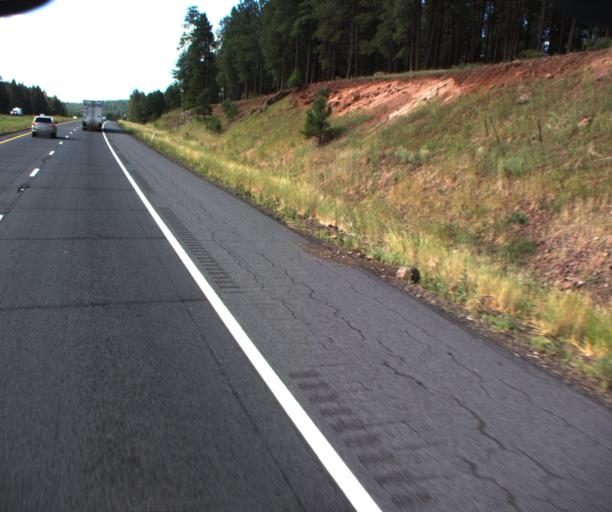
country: US
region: Arizona
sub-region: Coconino County
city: Mountainaire
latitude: 34.9667
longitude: -111.6823
